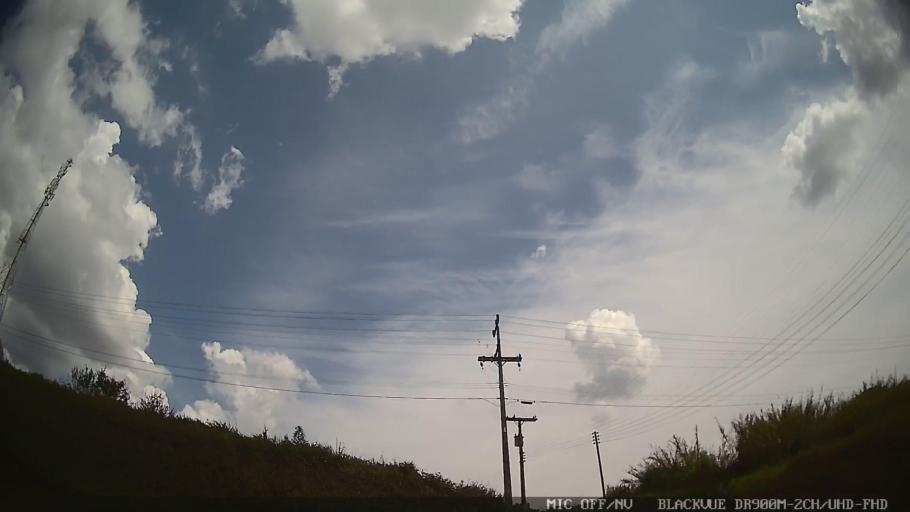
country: BR
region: Sao Paulo
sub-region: Jarinu
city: Jarinu
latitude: -22.9603
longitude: -46.7012
